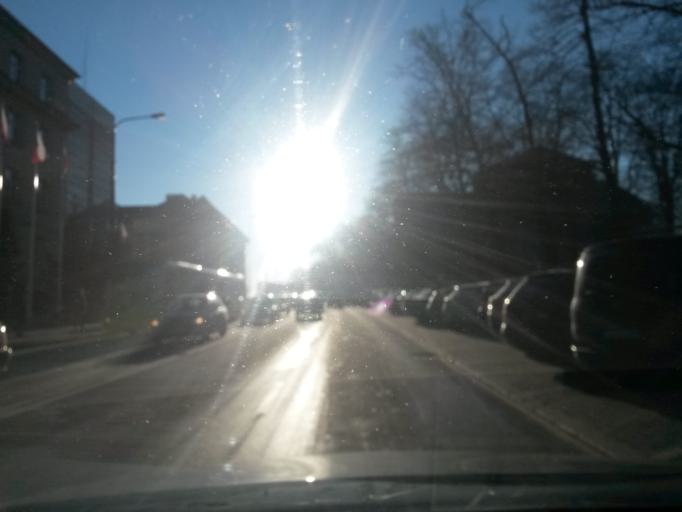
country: PL
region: Greater Poland Voivodeship
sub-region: Poznan
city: Poznan
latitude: 52.4113
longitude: 16.9190
